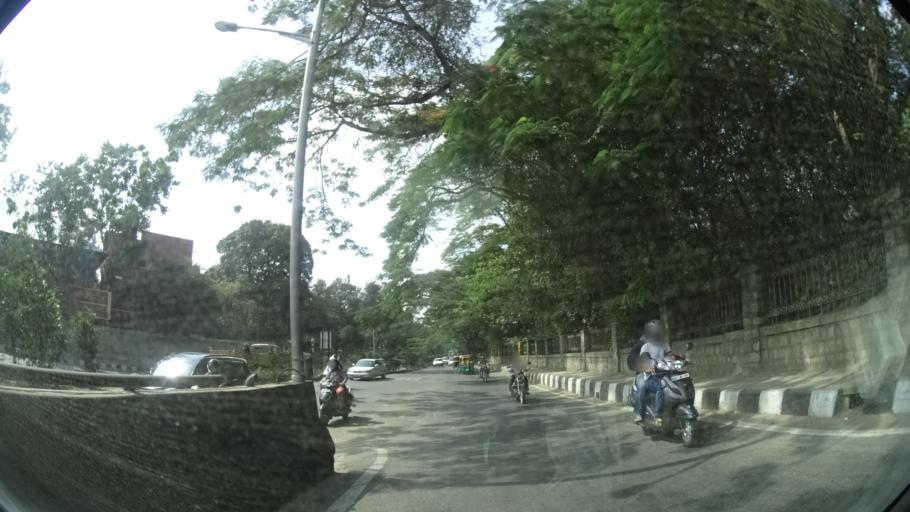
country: IN
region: Karnataka
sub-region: Bangalore Urban
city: Bangalore
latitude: 13.0149
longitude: 77.5645
